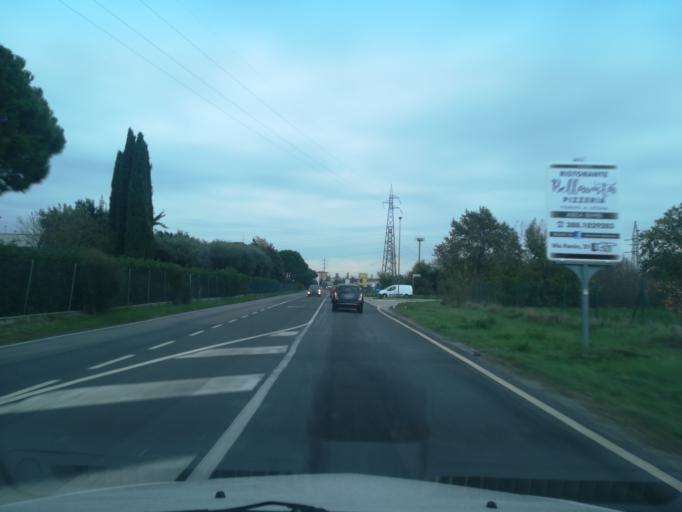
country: IT
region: Emilia-Romagna
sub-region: Provincia di Bologna
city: Imola
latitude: 44.3699
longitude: 11.7089
